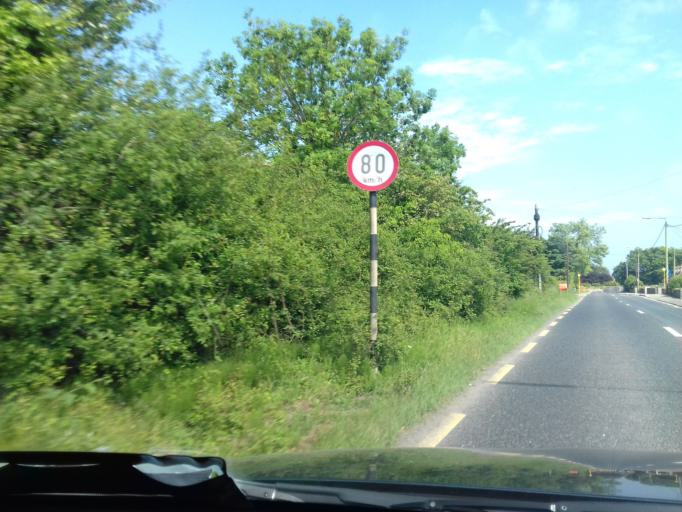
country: IE
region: Leinster
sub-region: Fingal County
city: Swords
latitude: 53.4724
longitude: -6.2530
